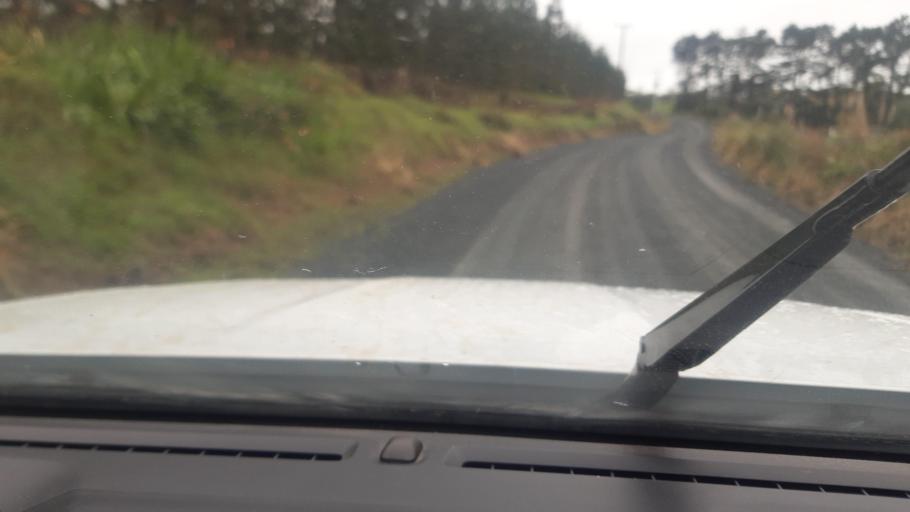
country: NZ
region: Northland
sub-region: Far North District
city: Kaitaia
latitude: -34.9789
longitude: 173.1986
